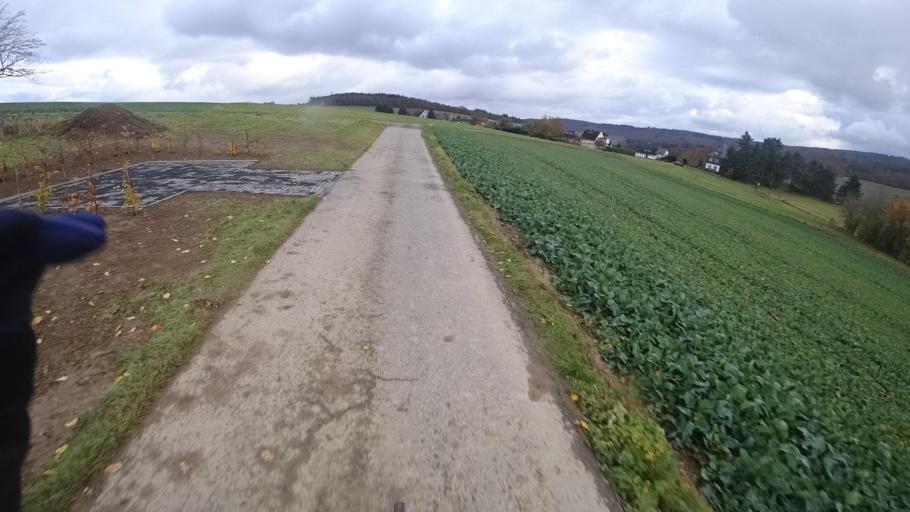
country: DE
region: Rheinland-Pfalz
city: Badenhard
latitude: 50.1239
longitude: 7.6266
